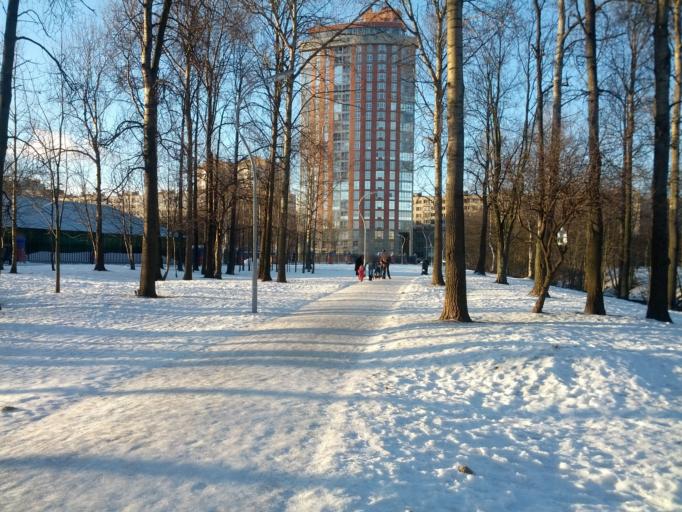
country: RU
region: St.-Petersburg
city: Krasnogvargeisky
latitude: 59.9133
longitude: 30.4843
